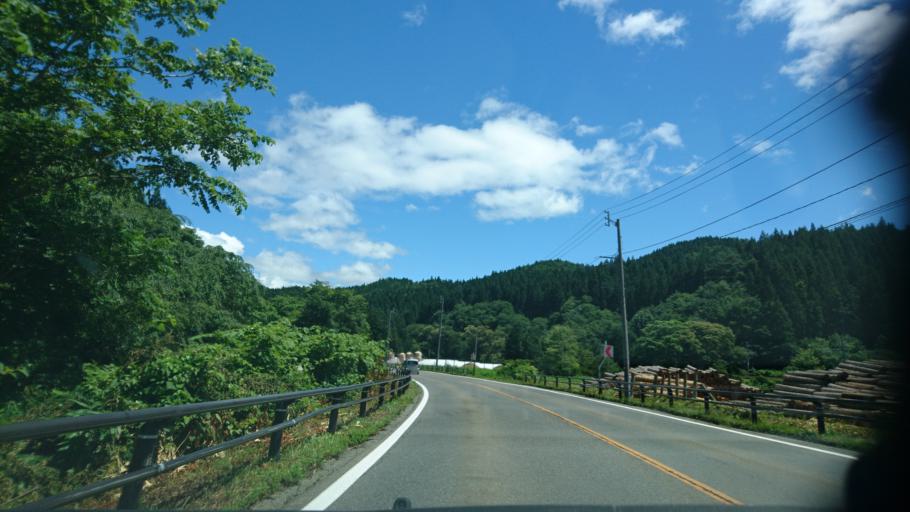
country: JP
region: Akita
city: Kakunodatemachi
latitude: 39.6530
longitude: 140.6713
